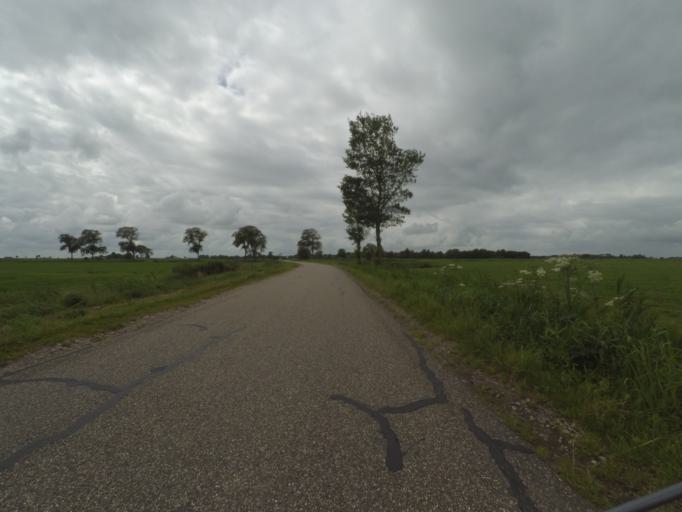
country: NL
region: Friesland
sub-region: Gemeente Kollumerland en Nieuwkruisland
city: Kollumerzwaag
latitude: 53.2991
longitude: 6.0849
